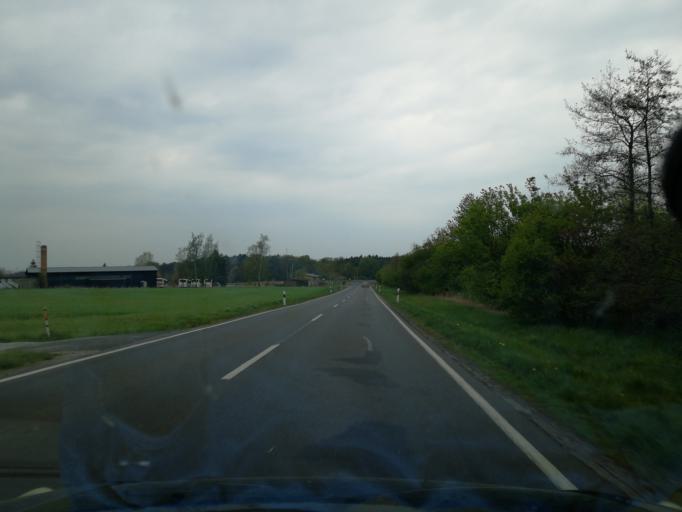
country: DE
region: Brandenburg
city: Calau
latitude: 51.7501
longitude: 13.9399
